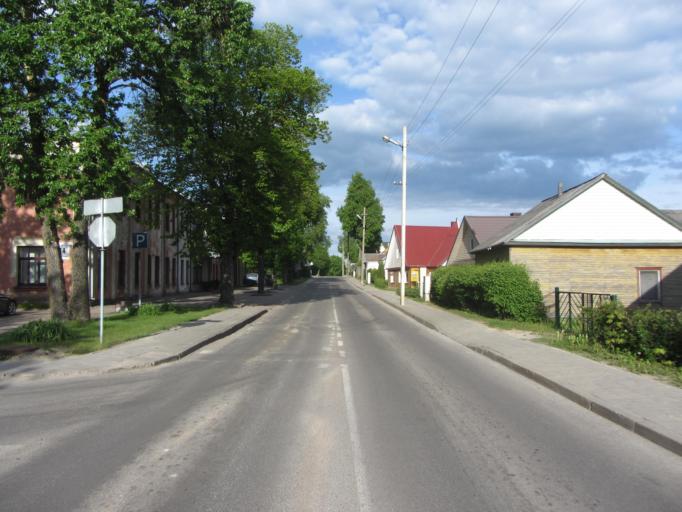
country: LT
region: Utenos apskritis
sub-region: Utena
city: Utena
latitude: 55.4980
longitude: 25.6070
